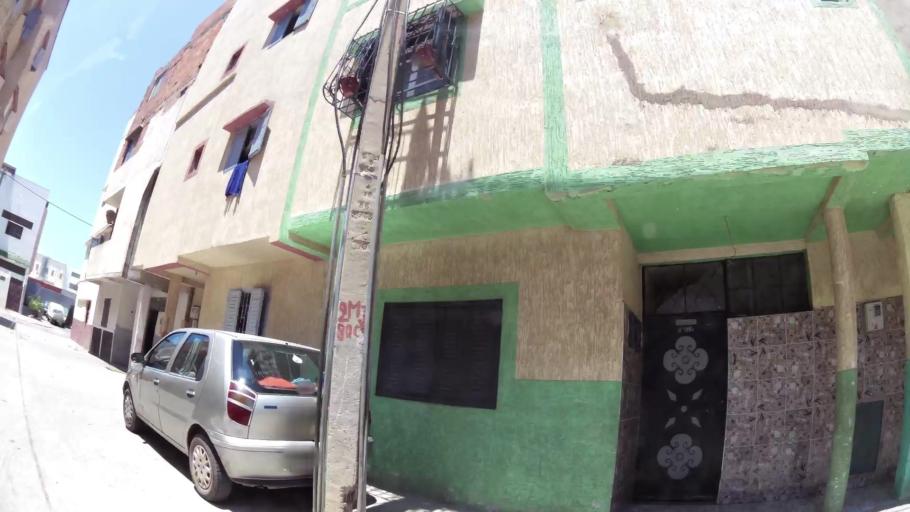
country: MA
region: Rabat-Sale-Zemmour-Zaer
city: Sale
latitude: 34.0670
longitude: -6.7907
